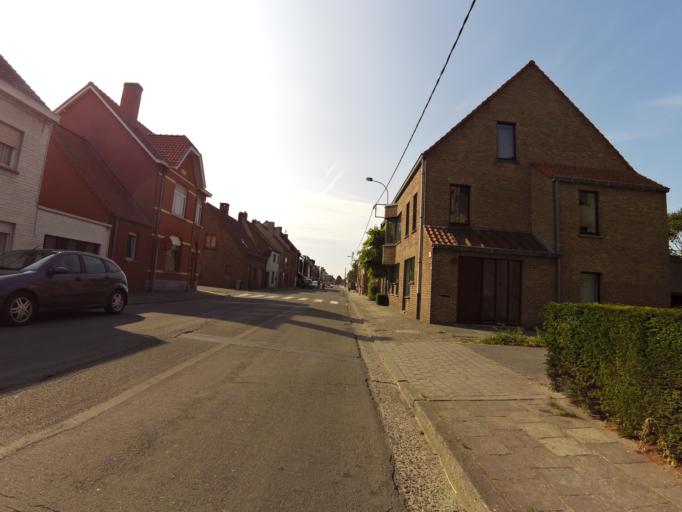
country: BE
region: Flanders
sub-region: Provincie West-Vlaanderen
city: Oudenburg
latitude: 51.1866
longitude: 2.9979
